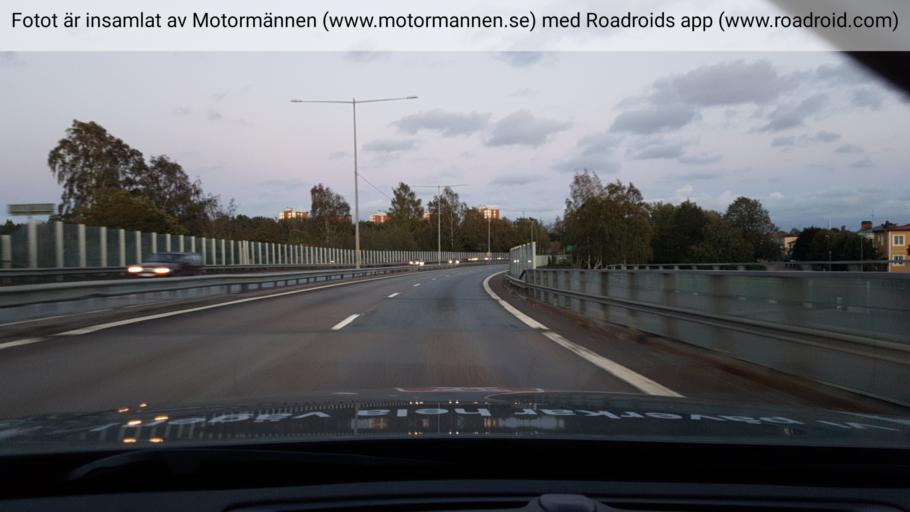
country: SE
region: Vaermland
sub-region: Karlstads Kommun
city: Karlstad
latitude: 59.3980
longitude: 13.5064
